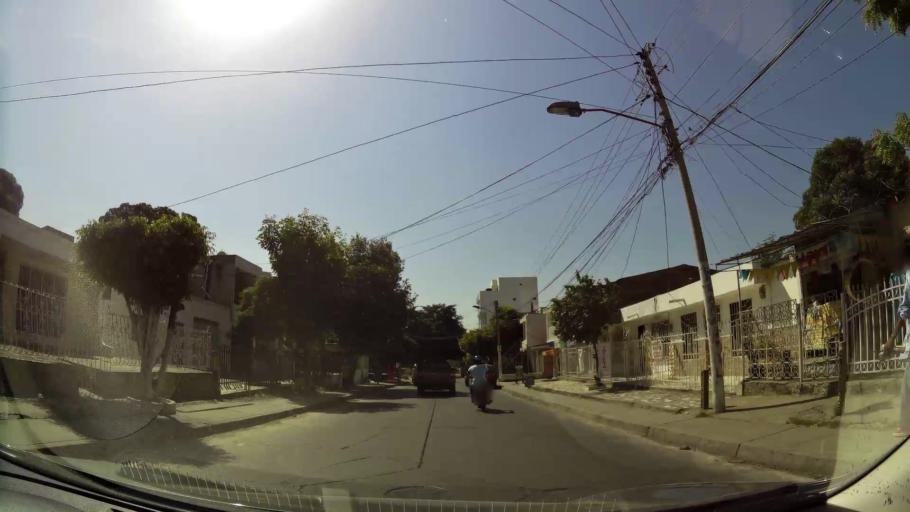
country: CO
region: Bolivar
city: Cartagena
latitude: 10.3927
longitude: -75.5039
